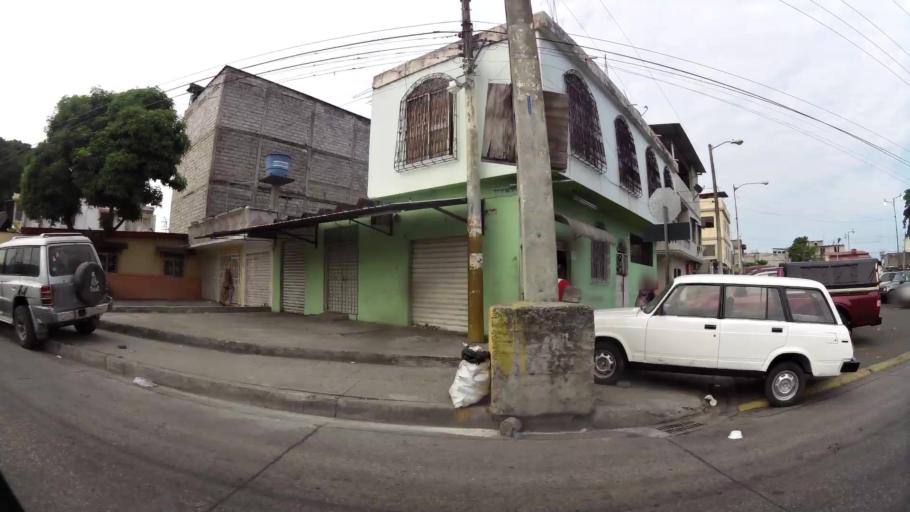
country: EC
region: Guayas
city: Guayaquil
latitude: -2.2509
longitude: -79.8866
